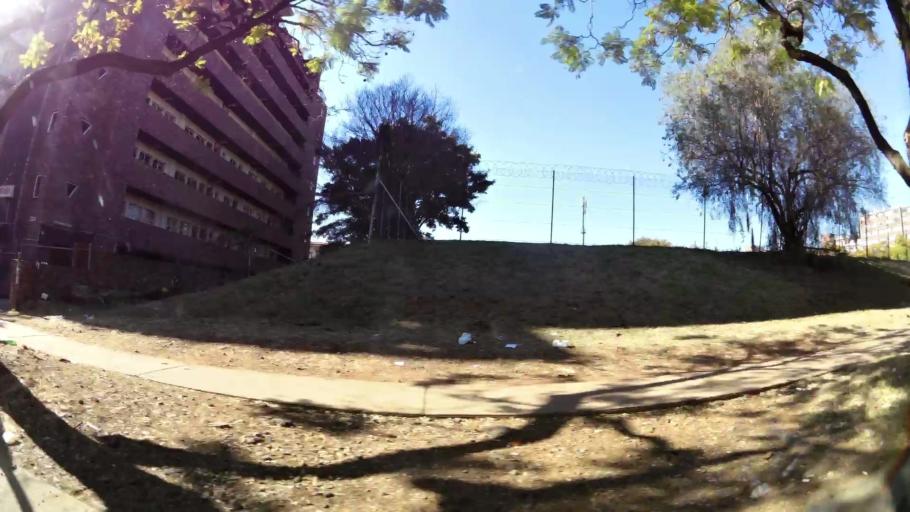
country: ZA
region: Gauteng
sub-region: City of Tshwane Metropolitan Municipality
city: Pretoria
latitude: -25.7572
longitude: 28.2061
